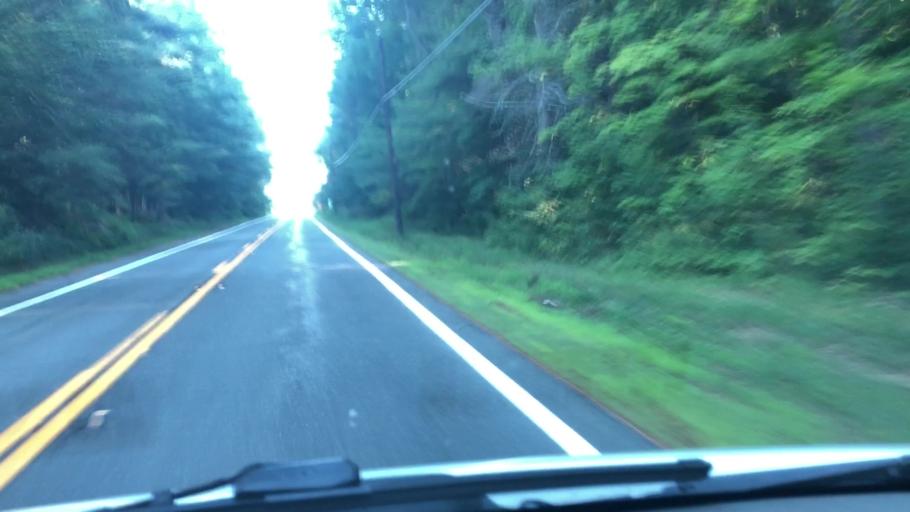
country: US
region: Massachusetts
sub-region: Hampshire County
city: Chesterfield
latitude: 42.3776
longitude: -72.9206
